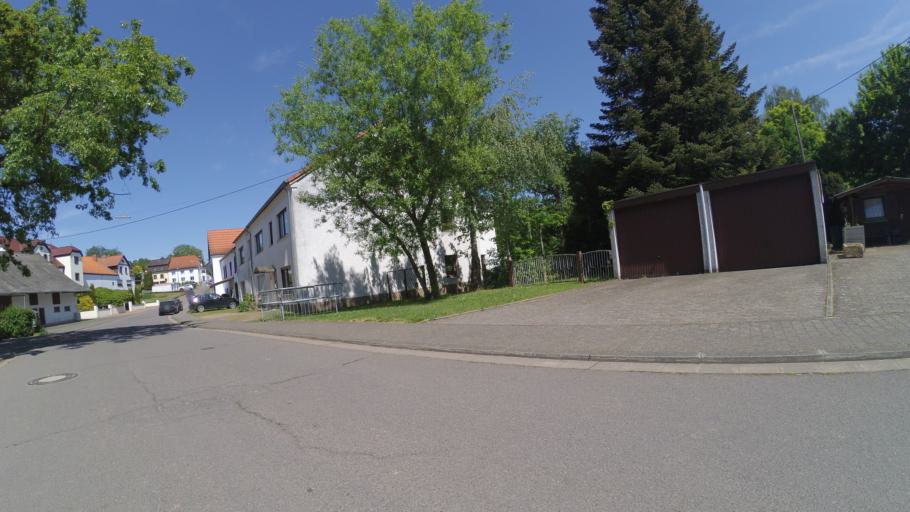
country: DE
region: Saarland
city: Heusweiler
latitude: 49.3445
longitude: 6.8943
